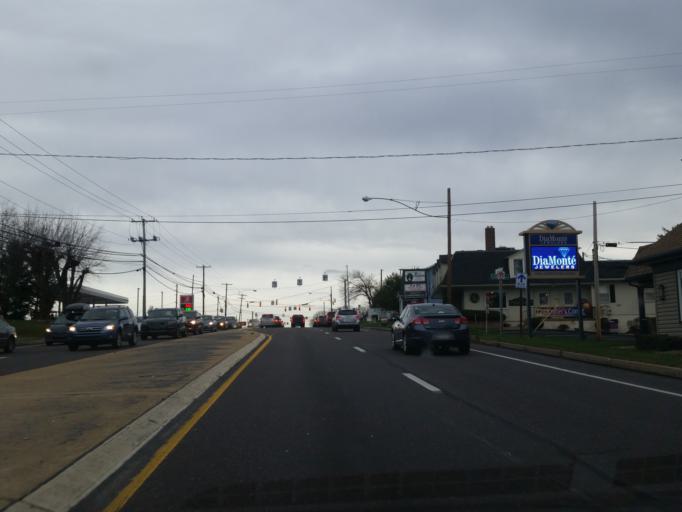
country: US
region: Pennsylvania
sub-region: Dauphin County
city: Paxtonia
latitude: 40.3150
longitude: -76.7980
